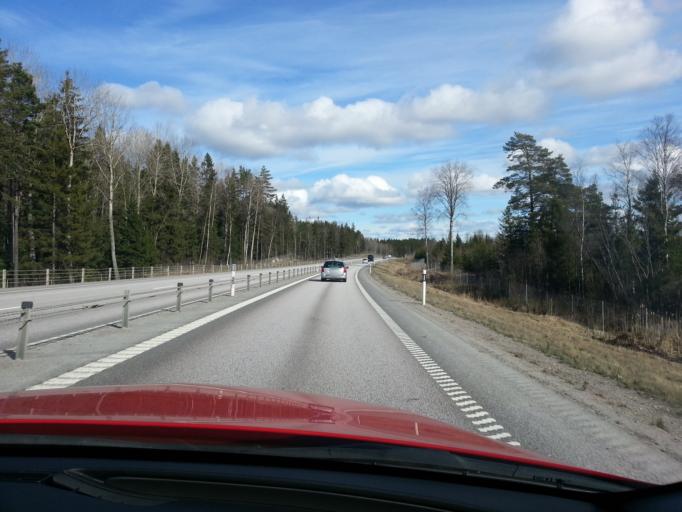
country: SE
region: Uppsala
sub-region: Uppsala Kommun
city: Storvreta
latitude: 59.9220
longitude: 17.7642
